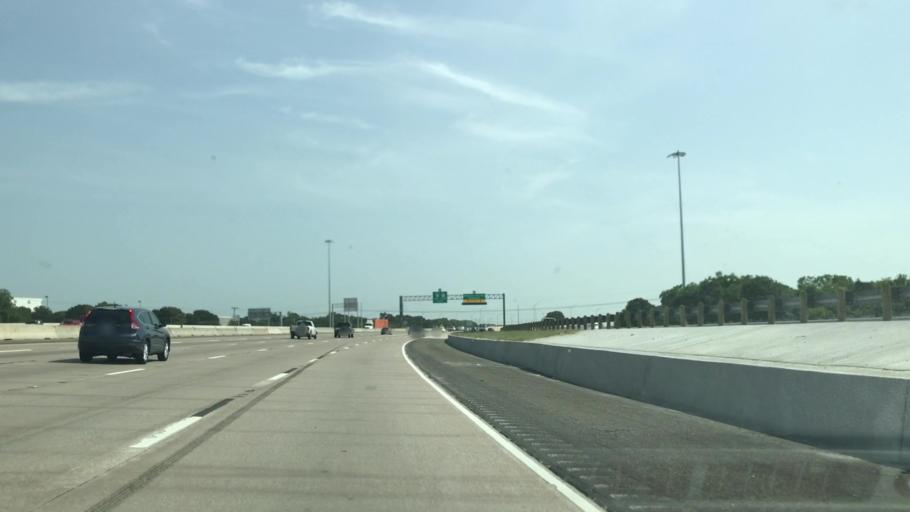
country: US
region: Texas
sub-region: Tarrant County
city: Grapevine
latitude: 32.9121
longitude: -97.0982
